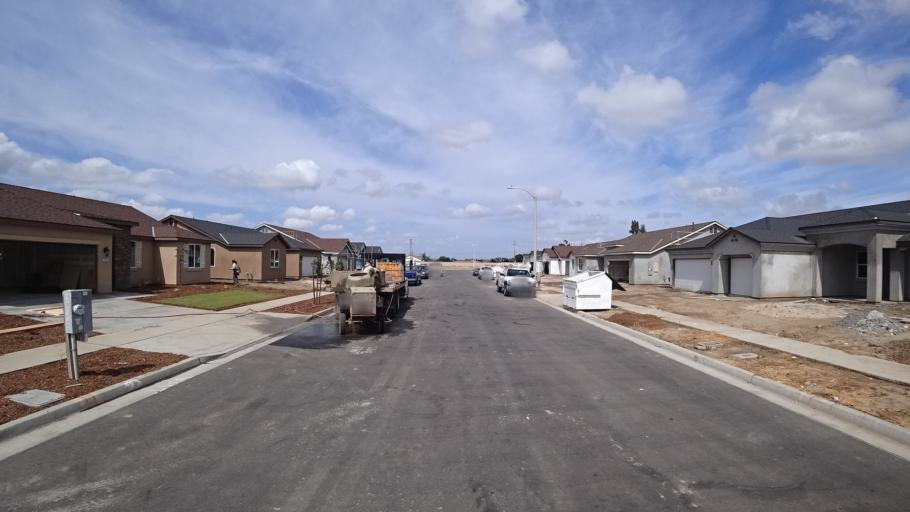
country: US
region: California
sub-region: Kings County
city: Hanford
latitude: 36.3085
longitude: -119.6710
